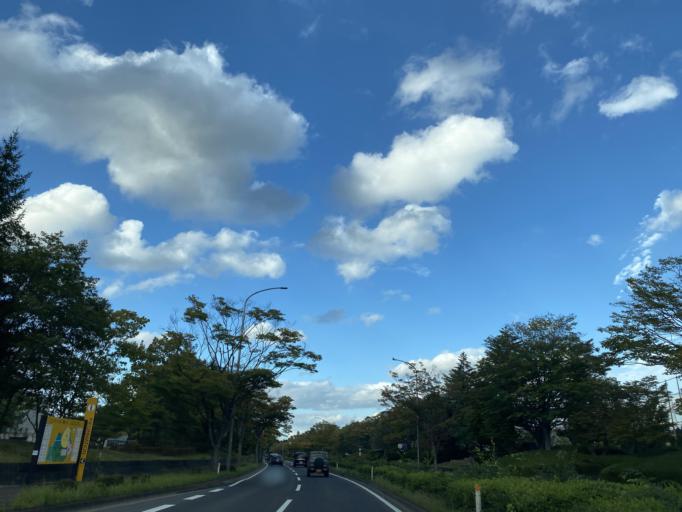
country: JP
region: Miyagi
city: Tomiya
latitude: 38.3489
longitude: 140.8421
